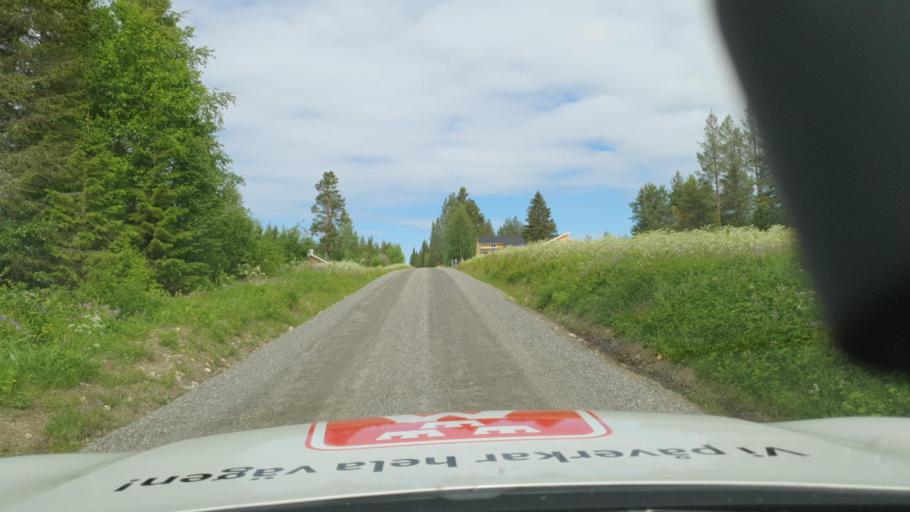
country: SE
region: Vaesterbotten
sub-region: Skelleftea Kommun
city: Langsele
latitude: 64.6191
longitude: 20.2664
